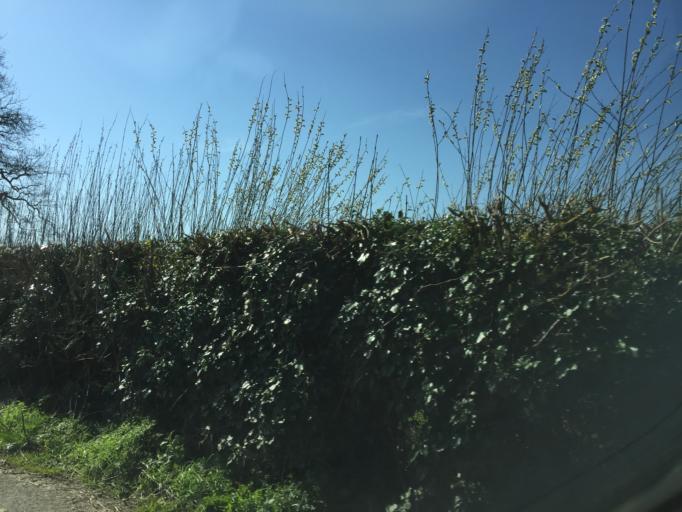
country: GB
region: England
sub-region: South Gloucestershire
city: Hill
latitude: 51.6421
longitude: -2.5079
